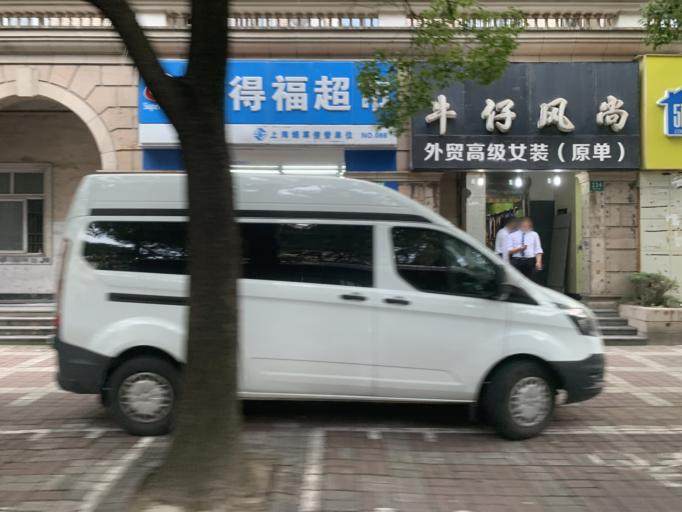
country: CN
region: Shanghai Shi
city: Pudong
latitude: 31.2480
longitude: 121.5488
